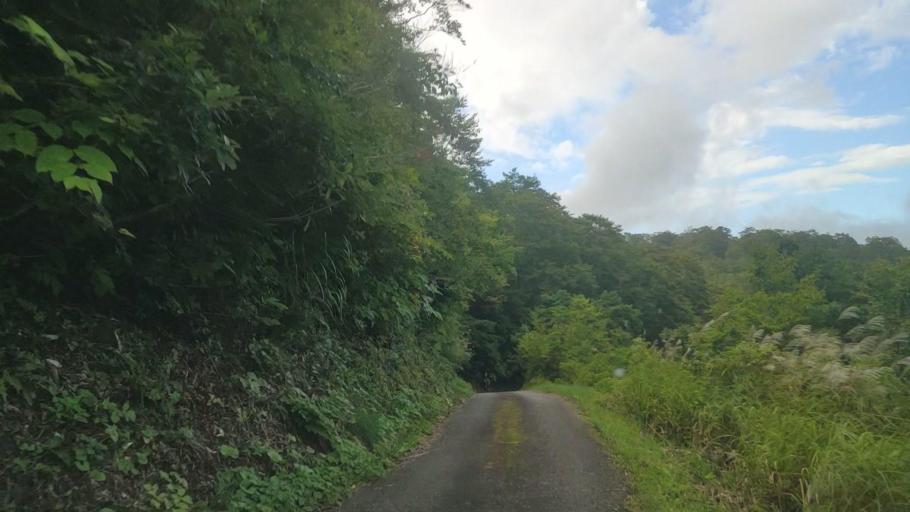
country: JP
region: Toyama
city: Yatsuomachi-higashikumisaka
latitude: 36.3550
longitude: 137.0642
